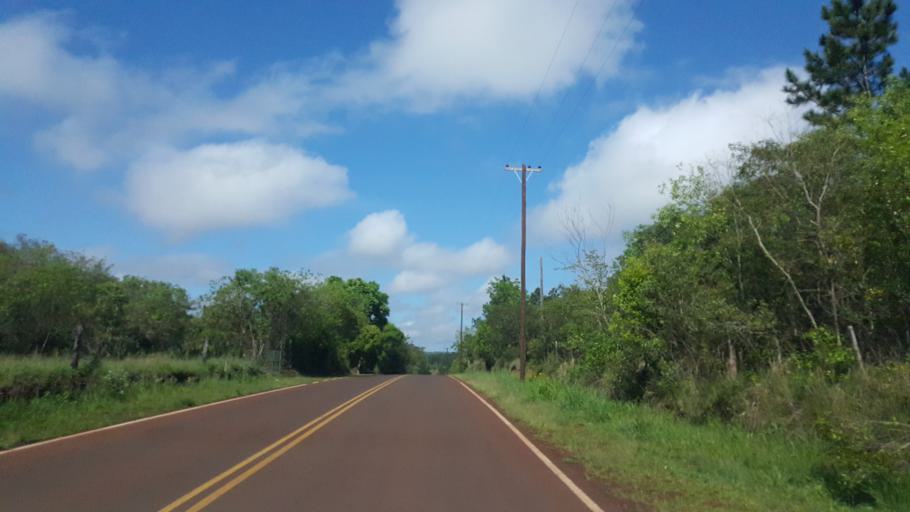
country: AR
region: Misiones
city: Garupa
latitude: -27.5021
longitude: -55.8500
